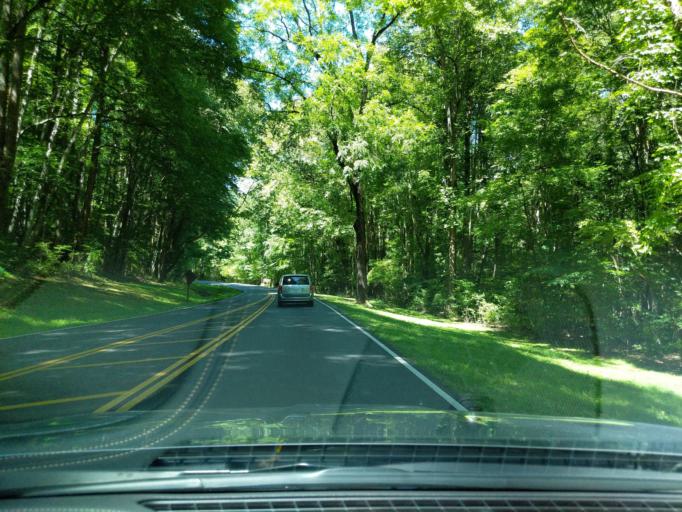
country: US
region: North Carolina
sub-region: Swain County
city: Cherokee
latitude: 35.5172
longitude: -83.3067
